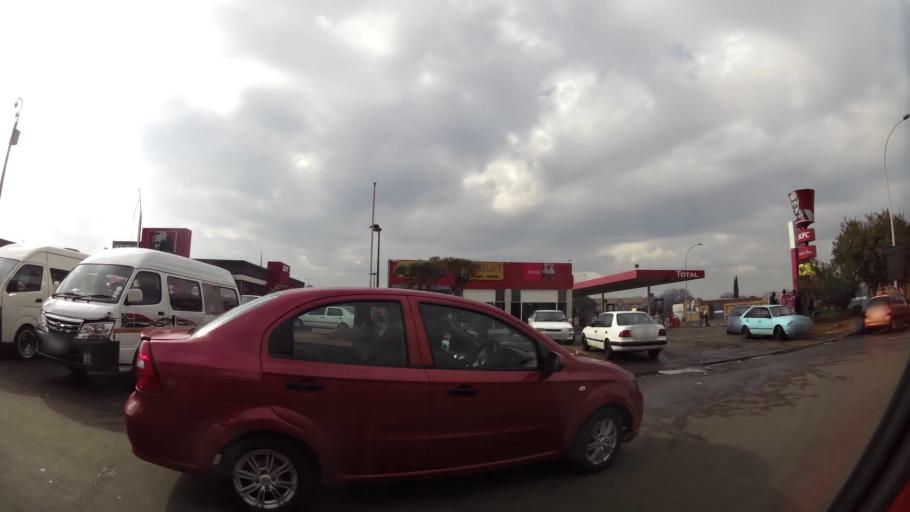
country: ZA
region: Gauteng
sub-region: Sedibeng District Municipality
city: Vanderbijlpark
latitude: -26.6972
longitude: 27.8388
